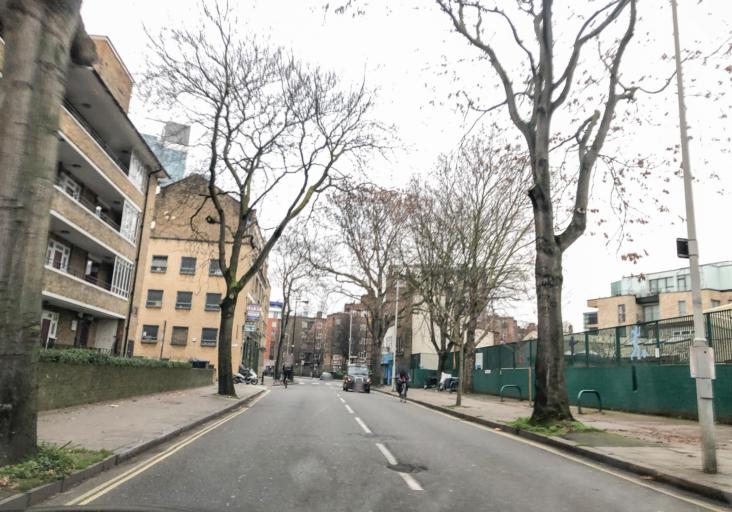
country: GB
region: England
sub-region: Greater London
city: City of London
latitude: 51.5003
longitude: -0.0881
